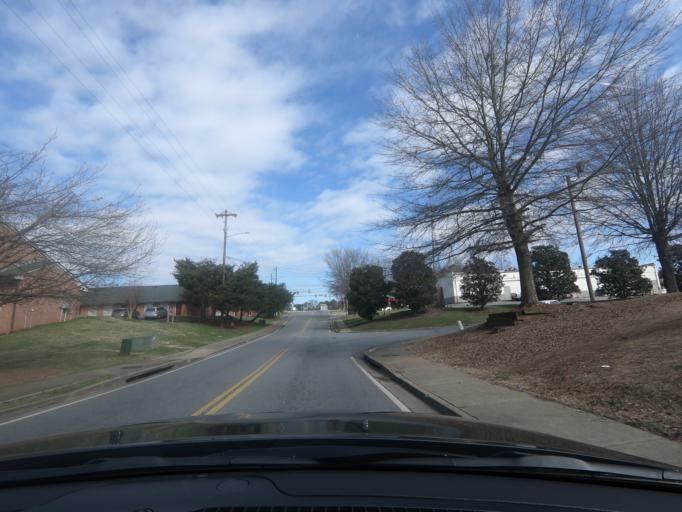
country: US
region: Georgia
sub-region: Cobb County
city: Acworth
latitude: 34.0745
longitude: -84.6497
